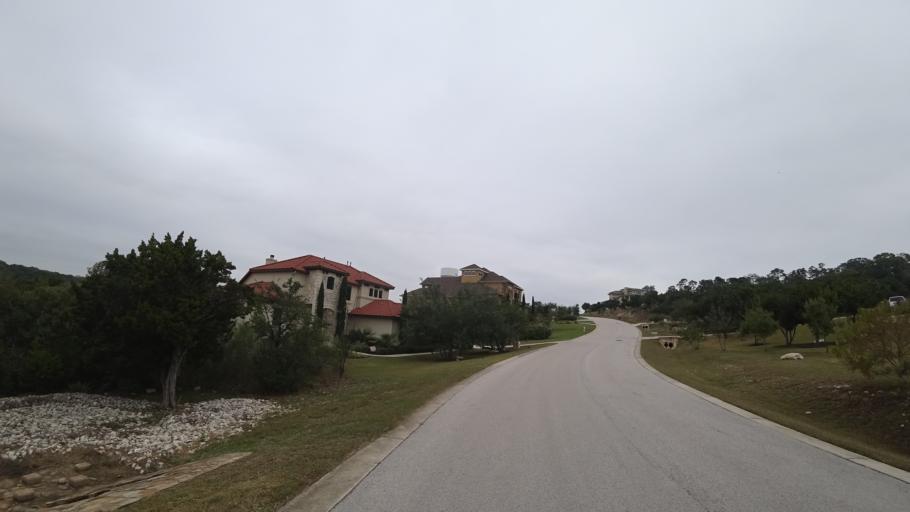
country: US
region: Texas
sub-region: Travis County
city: Hudson Bend
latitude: 30.3909
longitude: -97.9216
